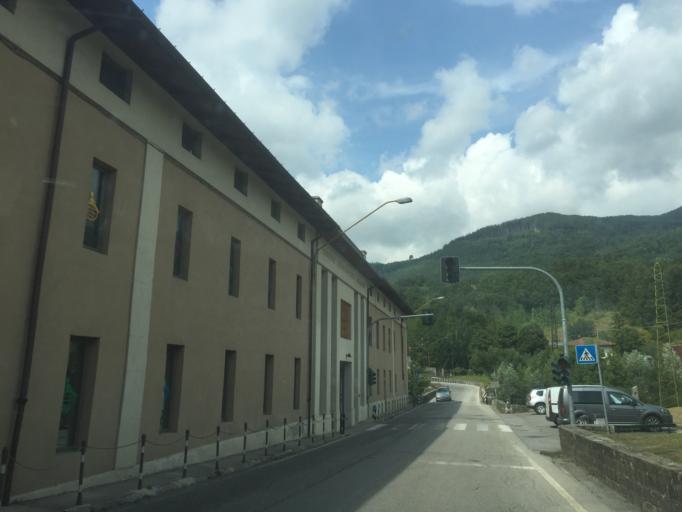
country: IT
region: Tuscany
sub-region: Provincia di Pistoia
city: San Marcello Pistoiese
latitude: 44.0471
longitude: 10.8084
